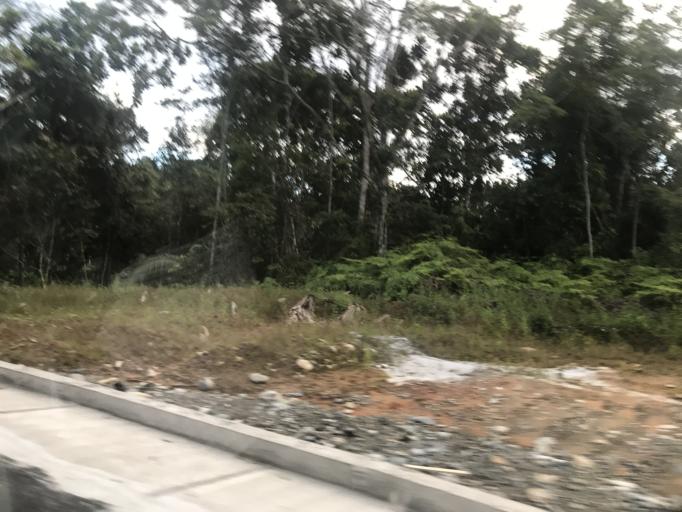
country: EC
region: Napo
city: Tena
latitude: -1.0639
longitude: -77.7021
